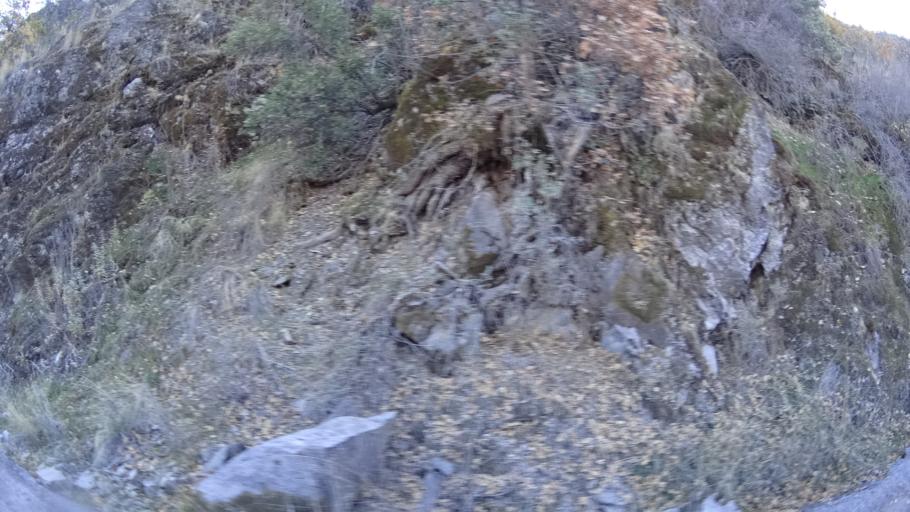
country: US
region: California
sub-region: Siskiyou County
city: Yreka
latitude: 41.8278
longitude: -122.6421
